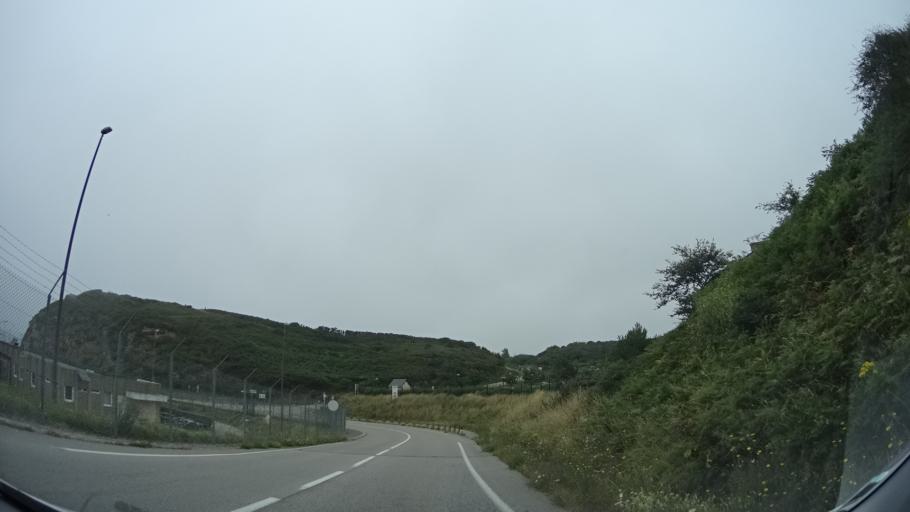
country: FR
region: Lower Normandy
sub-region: Departement de la Manche
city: Flamanville
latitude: 49.5424
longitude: -1.8736
